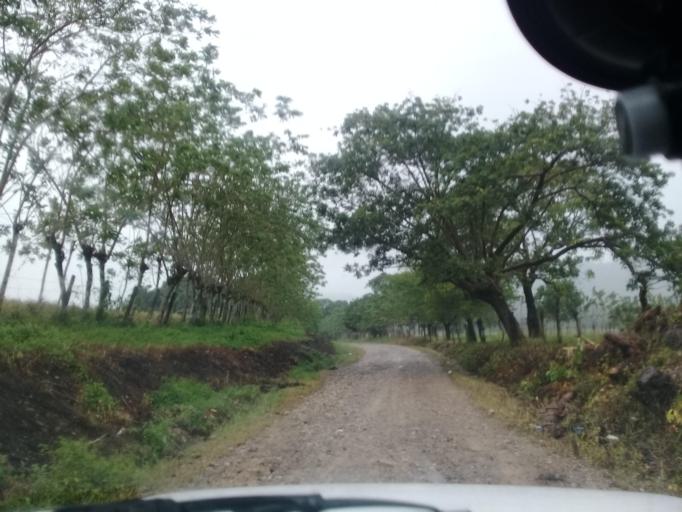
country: MX
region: Veracruz
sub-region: Chalma
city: San Pedro Coyutla
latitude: 21.2387
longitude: -98.4610
